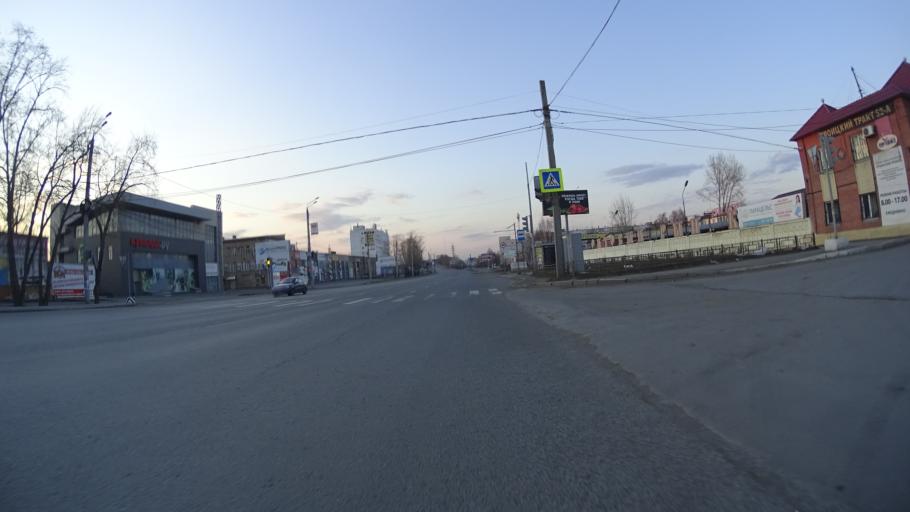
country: RU
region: Chelyabinsk
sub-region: Gorod Chelyabinsk
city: Chelyabinsk
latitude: 55.1106
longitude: 61.3870
